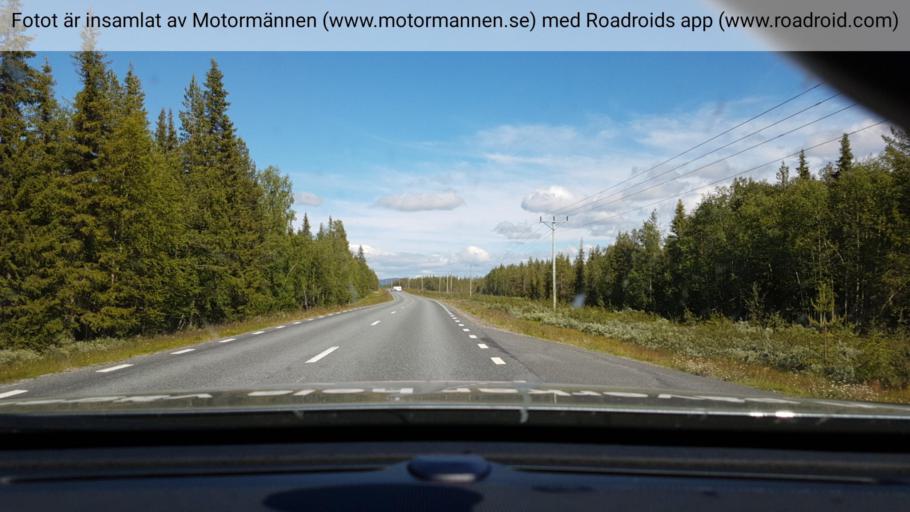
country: SE
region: Norrbotten
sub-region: Arjeplogs Kommun
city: Arjeplog
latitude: 65.5776
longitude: 18.0791
